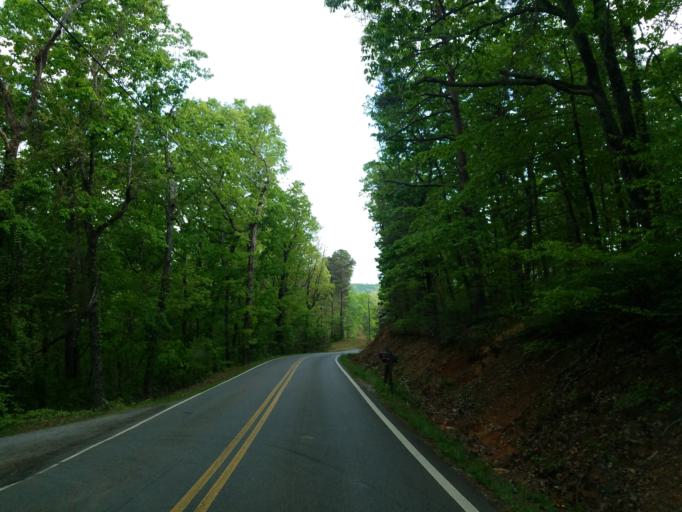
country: US
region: Georgia
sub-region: Pickens County
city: Jasper
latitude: 34.4408
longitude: -84.4726
